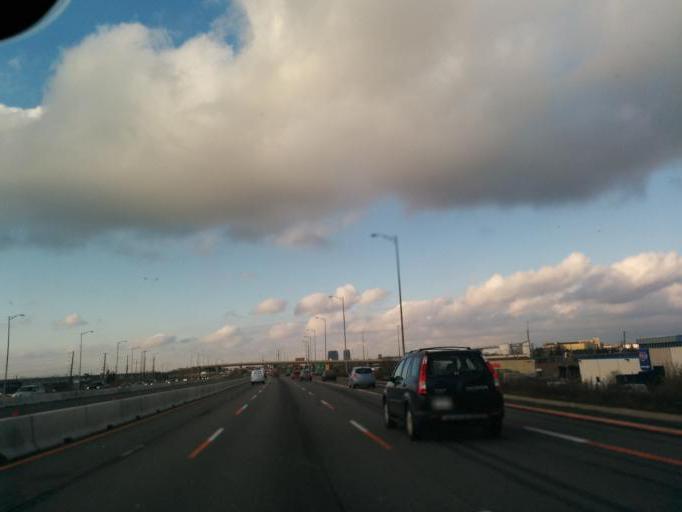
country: CA
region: Ontario
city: Etobicoke
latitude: 43.6916
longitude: -79.6038
